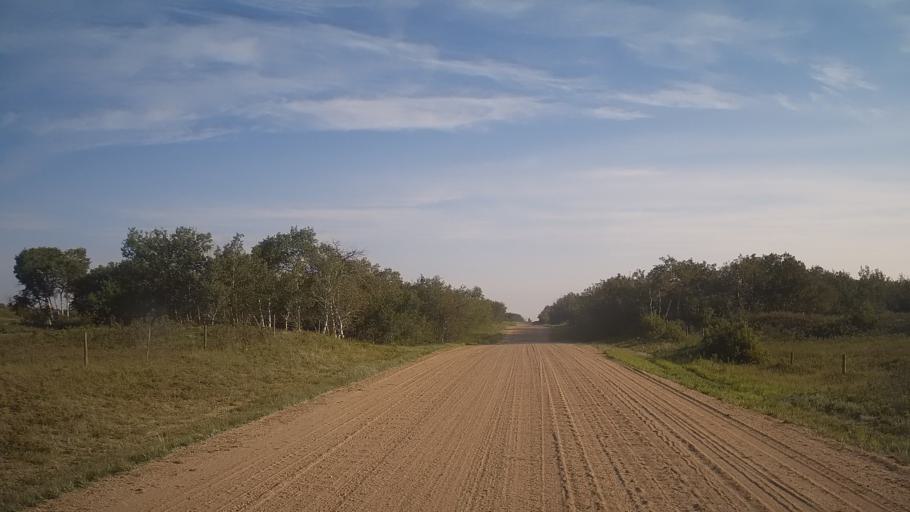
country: CA
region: Saskatchewan
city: Saskatoon
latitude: 51.8364
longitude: -106.5239
